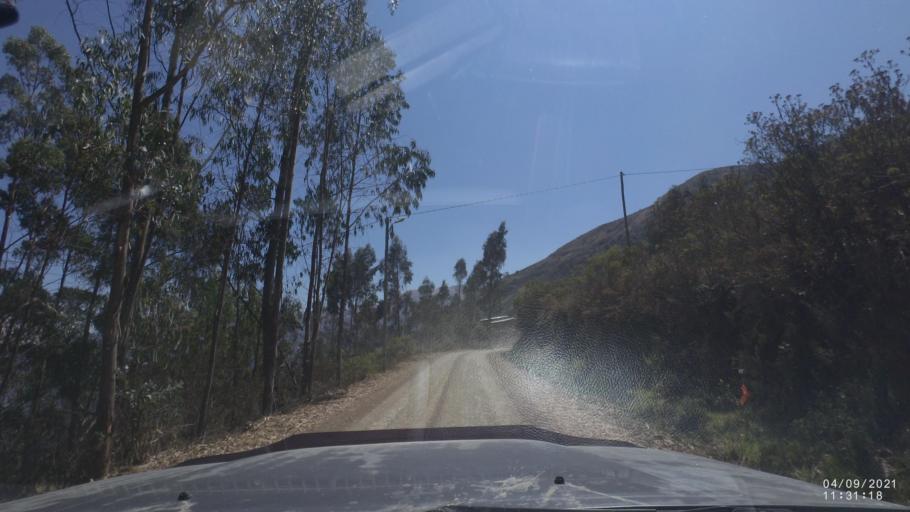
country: BO
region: Cochabamba
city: Colchani
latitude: -17.2335
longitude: -66.5213
